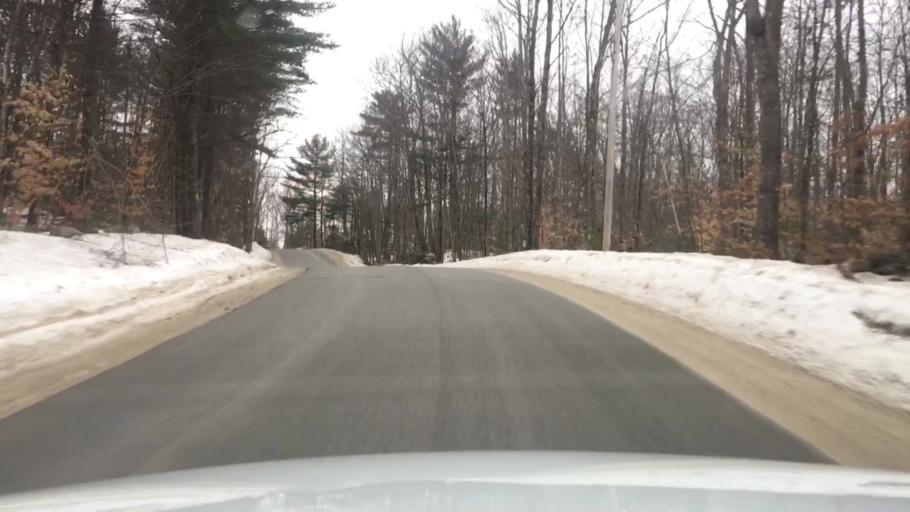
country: US
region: Maine
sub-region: York County
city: Springvale
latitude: 43.5024
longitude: -70.8210
